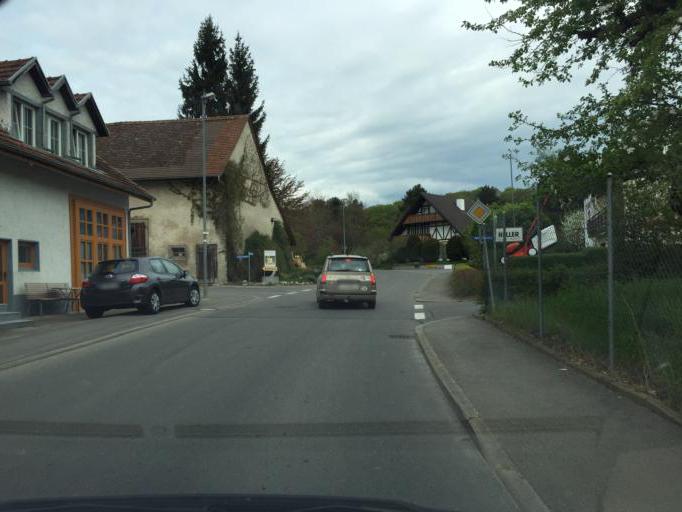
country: DE
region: Baden-Wuerttemberg
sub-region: Freiburg Region
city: Busingen
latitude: 47.6981
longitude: 8.6899
